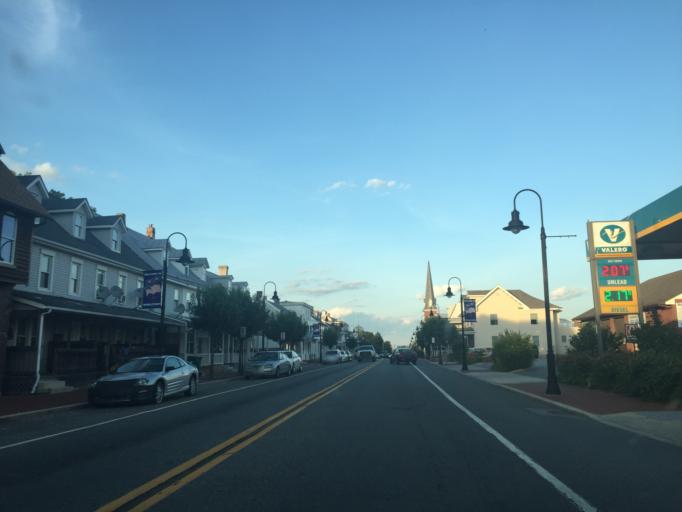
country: US
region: Delaware
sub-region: New Castle County
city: Middletown
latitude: 39.4497
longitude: -75.7160
